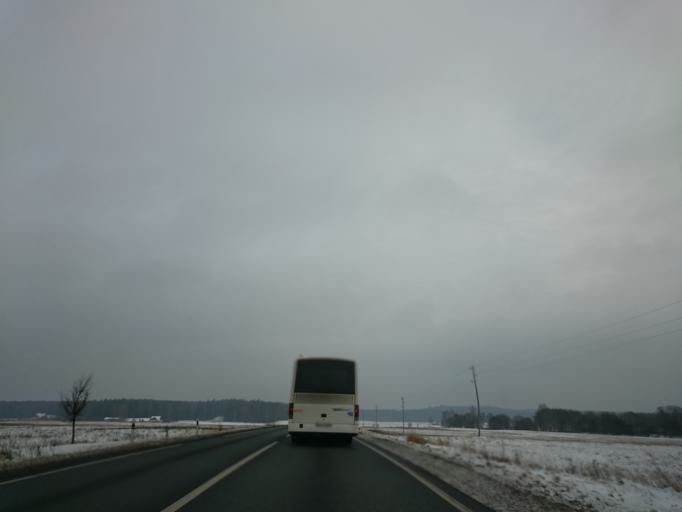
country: LV
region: Sigulda
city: Sigulda
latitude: 57.2646
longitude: 24.8785
